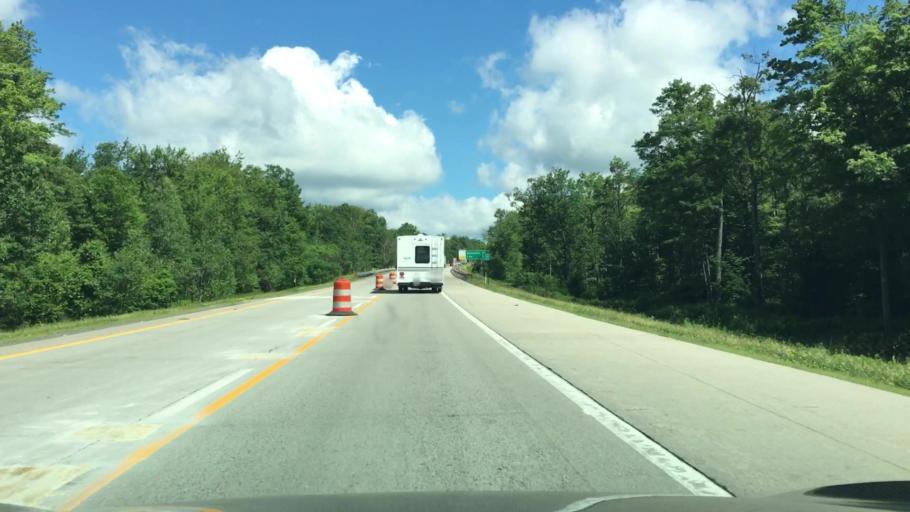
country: US
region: Pennsylvania
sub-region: Lackawanna County
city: Moscow
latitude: 41.2427
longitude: -75.5126
